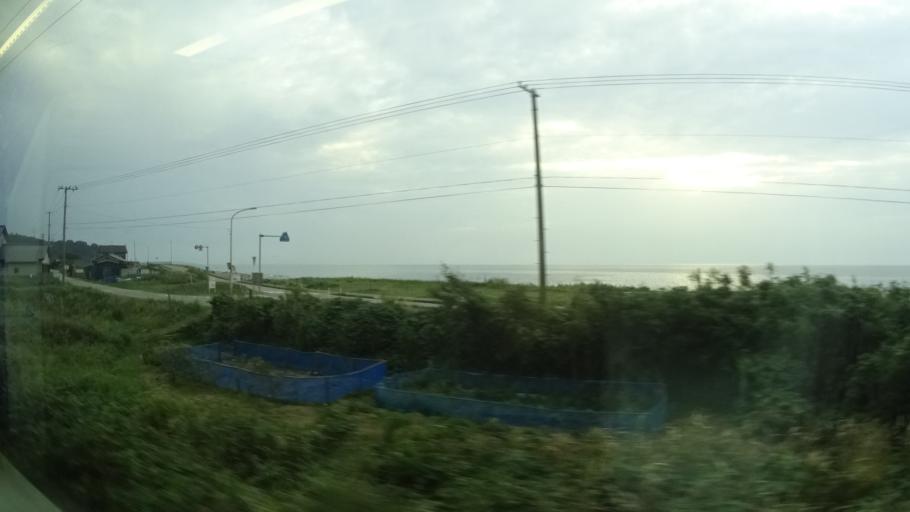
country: JP
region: Niigata
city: Murakami
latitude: 38.2805
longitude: 139.4502
